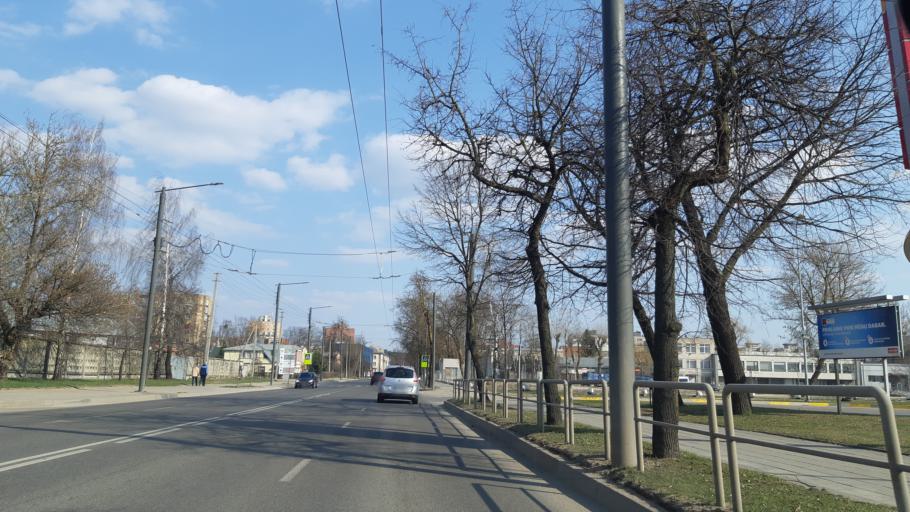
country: LT
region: Kauno apskritis
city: Dainava (Kaunas)
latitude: 54.8933
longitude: 23.9956
